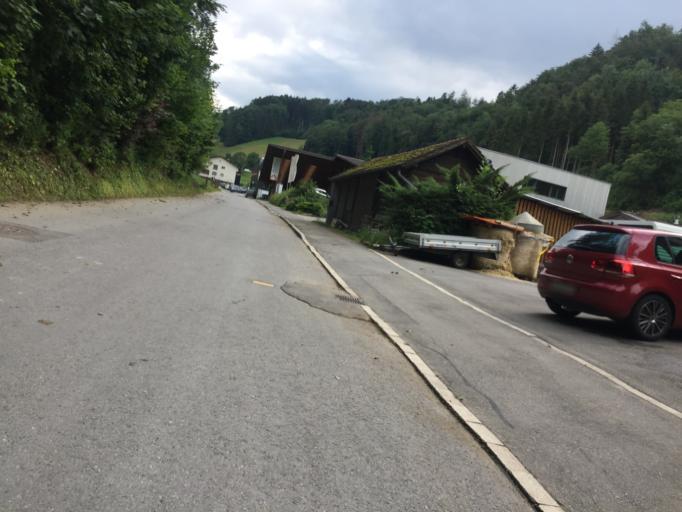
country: CH
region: Bern
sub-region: Bern-Mittelland District
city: Stettlen
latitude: 46.9548
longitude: 7.5118
